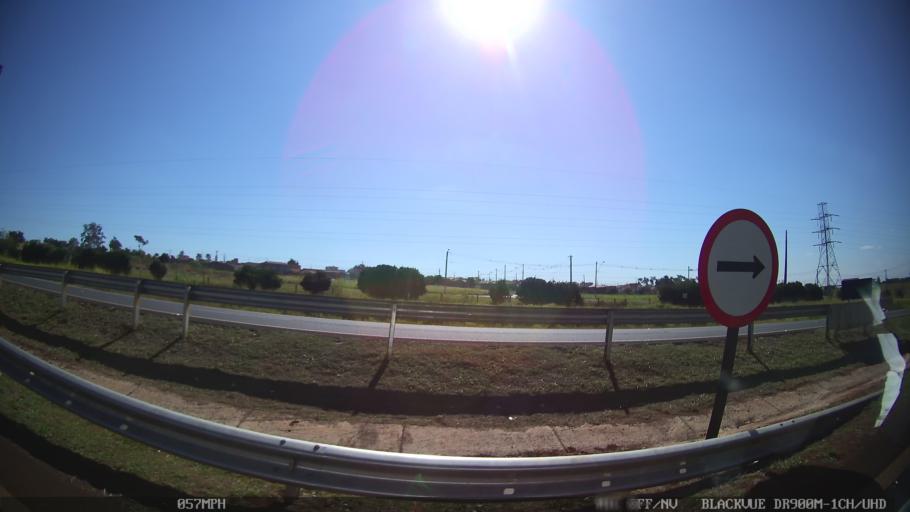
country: BR
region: Sao Paulo
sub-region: Ribeirao Preto
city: Ribeirao Preto
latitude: -21.1207
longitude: -47.8337
